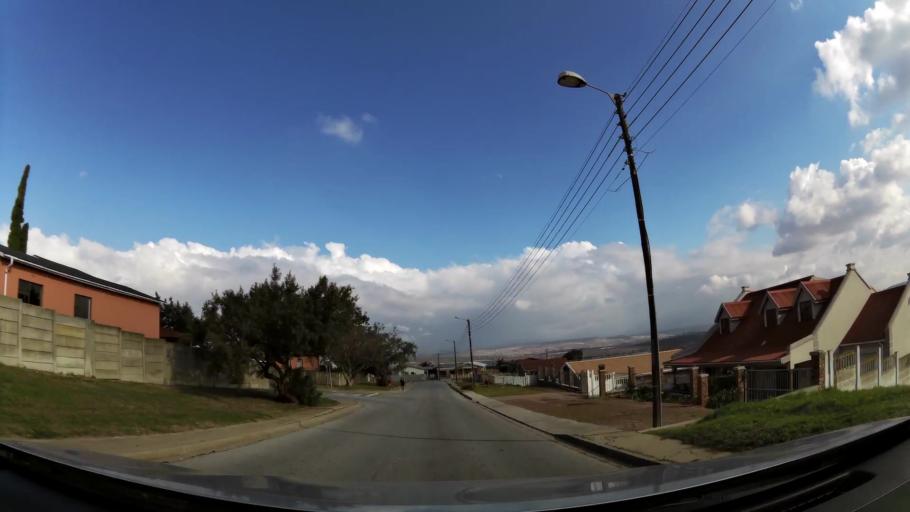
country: ZA
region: Eastern Cape
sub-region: Nelson Mandela Bay Metropolitan Municipality
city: Uitenhage
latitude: -33.7758
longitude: 25.4272
